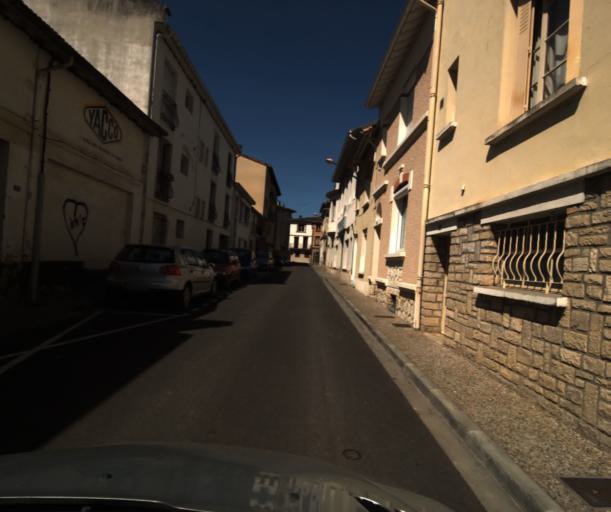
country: FR
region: Midi-Pyrenees
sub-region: Departement du Tarn-et-Garonne
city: Moissac
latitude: 44.1039
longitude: 1.0890
